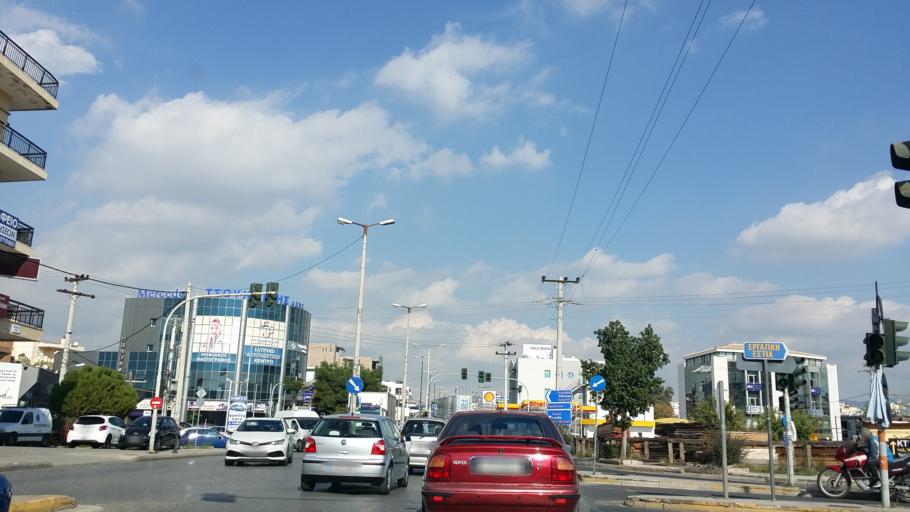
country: GR
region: Attica
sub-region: Nomarchia Athinas
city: Irakleio
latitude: 38.0502
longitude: 23.7491
